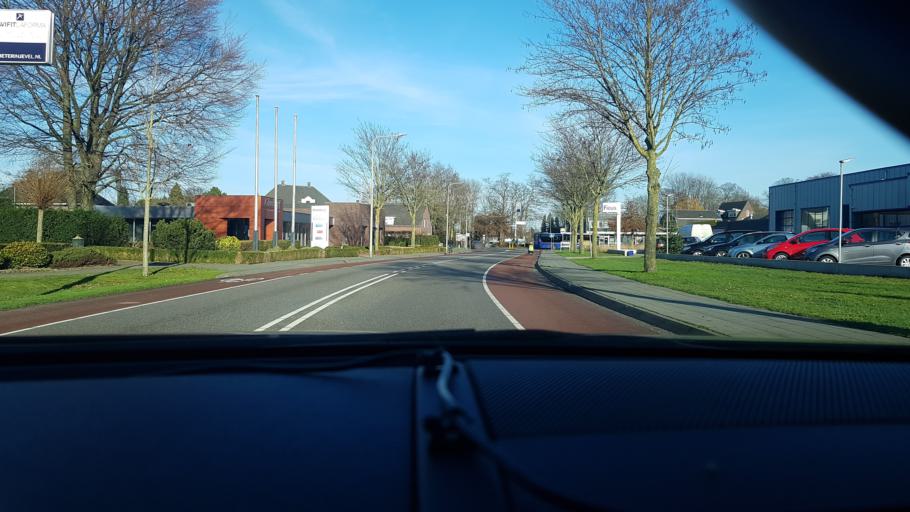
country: NL
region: Limburg
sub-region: Gemeente Peel en Maas
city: Maasbree
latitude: 51.3299
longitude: 5.9713
